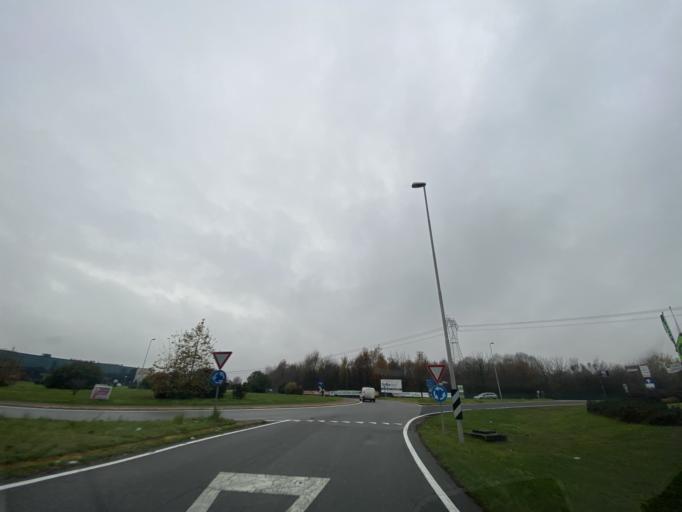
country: IT
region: Lombardy
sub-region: Citta metropolitana di Milano
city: Cusago
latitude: 45.4448
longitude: 9.0407
